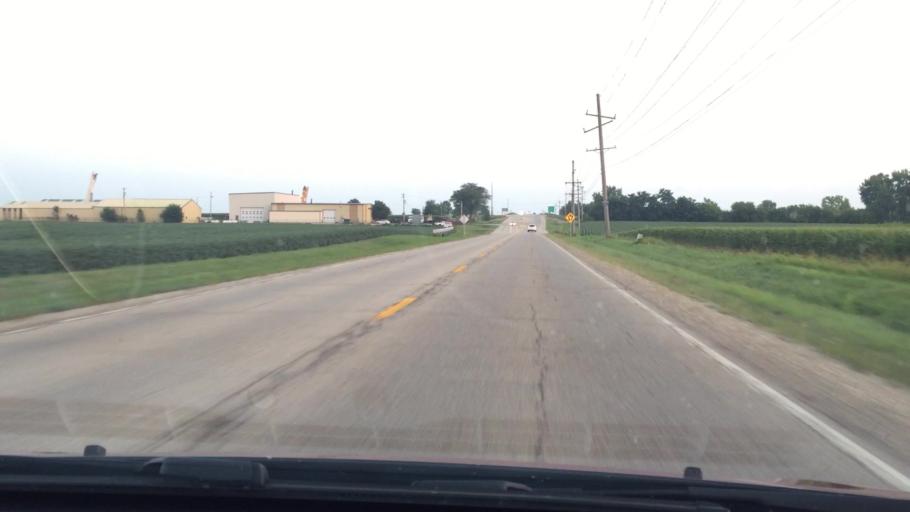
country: US
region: Illinois
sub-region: Bureau County
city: Ladd
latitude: 41.3751
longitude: -89.2190
